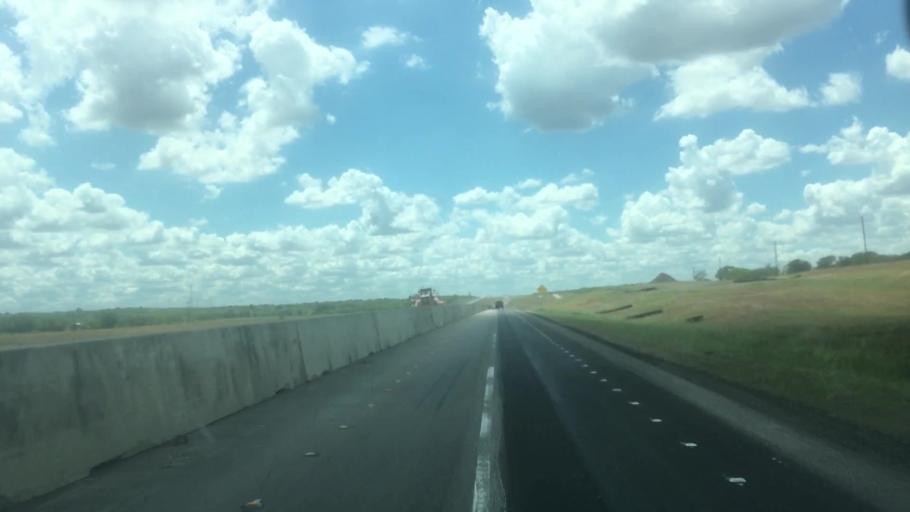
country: US
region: Texas
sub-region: Caldwell County
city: Lockhart
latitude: 29.8326
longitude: -97.7384
